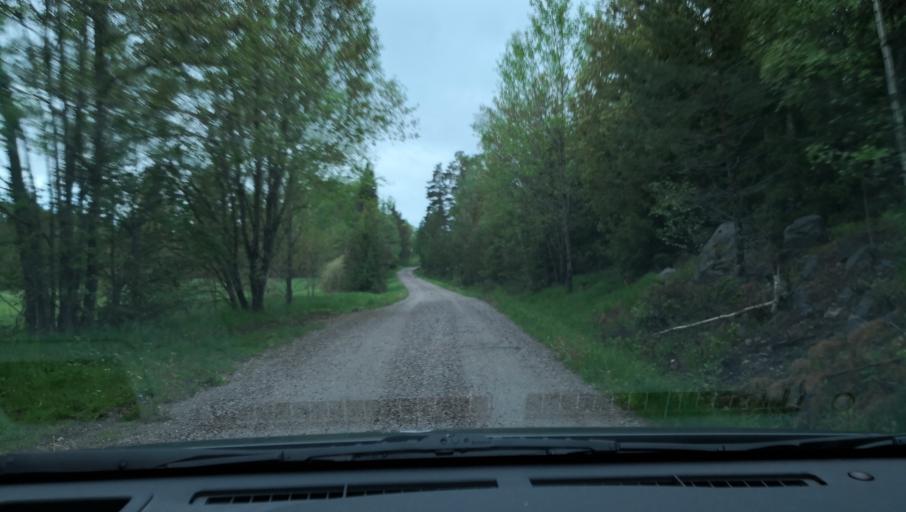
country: SE
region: Uppsala
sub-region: Heby Kommun
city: OEstervala
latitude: 59.9943
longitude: 17.2487
